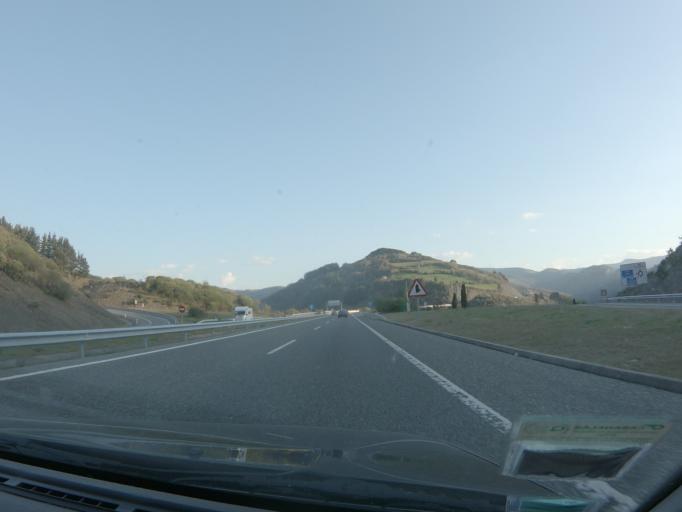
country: ES
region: Galicia
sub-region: Provincia de Lugo
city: San Roman
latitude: 42.8130
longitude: -7.1055
